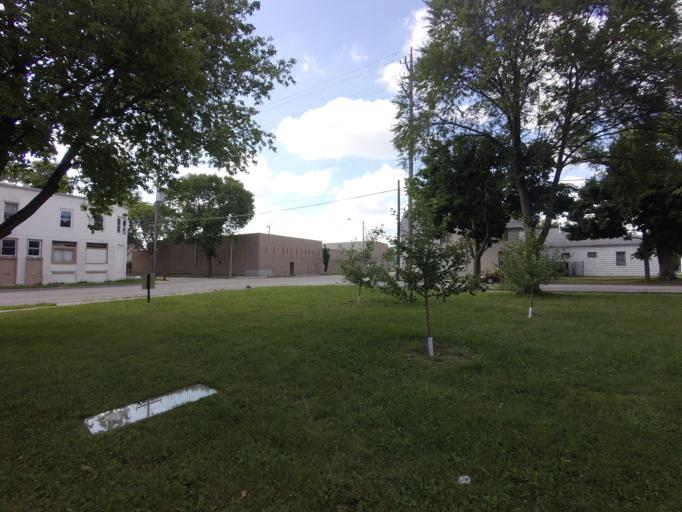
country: US
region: Wisconsin
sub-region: Milwaukee County
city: Shorewood
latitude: 43.0853
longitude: -87.9170
